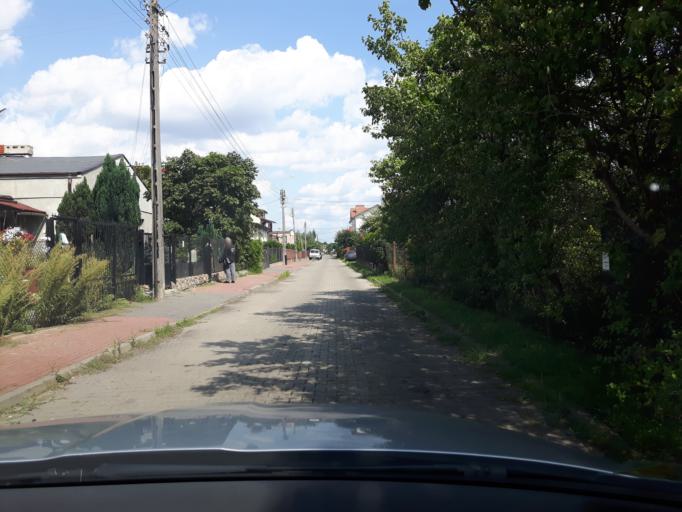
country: PL
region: Masovian Voivodeship
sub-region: Powiat wolominski
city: Zabki
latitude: 52.2894
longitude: 21.0979
